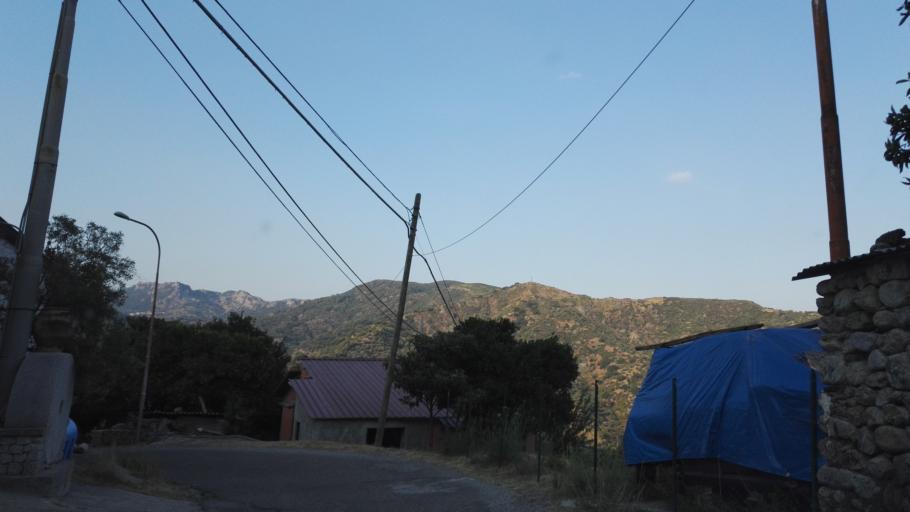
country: IT
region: Calabria
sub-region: Provincia di Reggio Calabria
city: Caulonia
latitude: 38.4126
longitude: 16.3702
